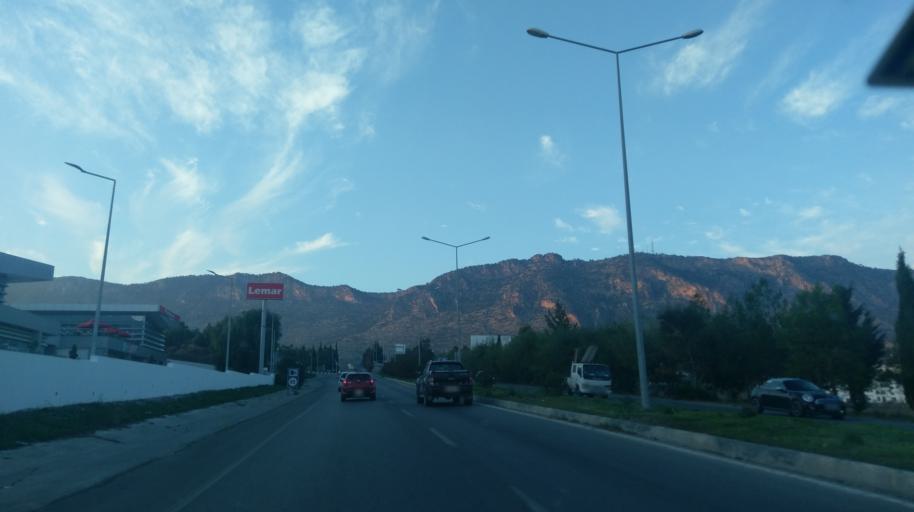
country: CY
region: Keryneia
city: Kyrenia
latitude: 35.2820
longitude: 33.2817
